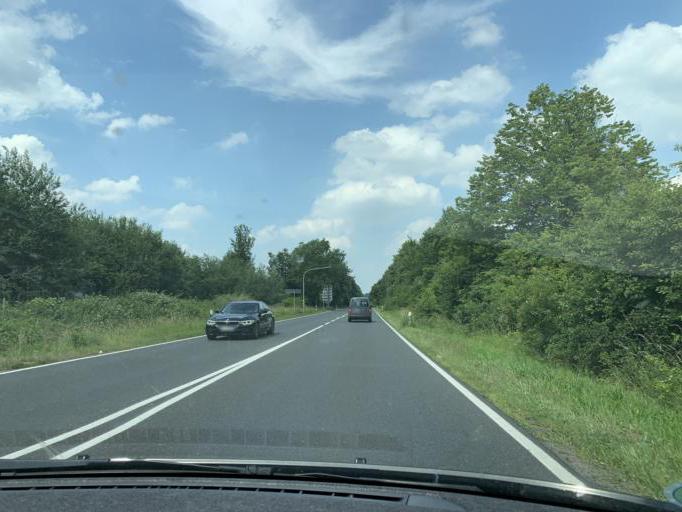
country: DE
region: North Rhine-Westphalia
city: Niedermerz
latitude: 50.8533
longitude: 6.2347
